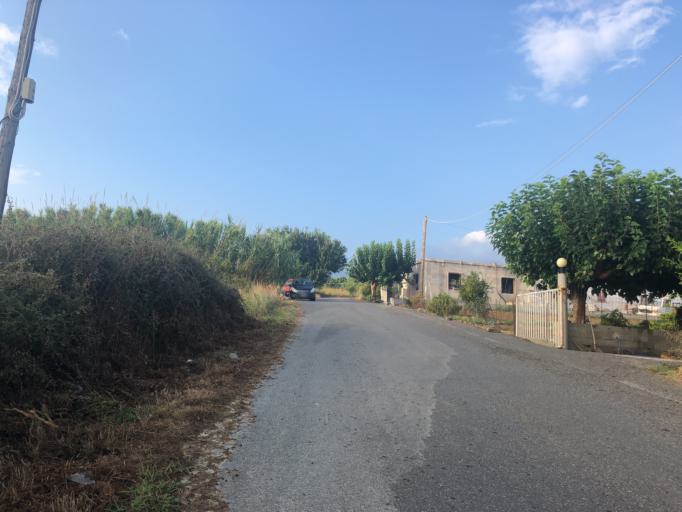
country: GR
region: Crete
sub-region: Nomos Chanias
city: Georgioupolis
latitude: 35.3482
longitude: 24.3148
